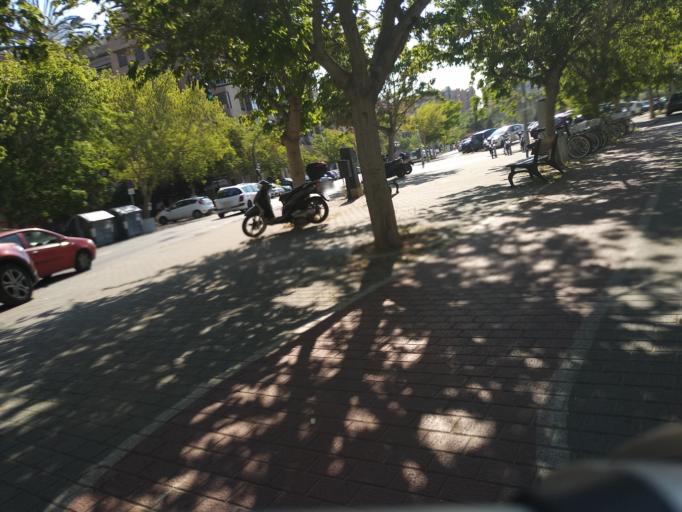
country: ES
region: Valencia
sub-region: Provincia de Valencia
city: Alboraya
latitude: 39.4784
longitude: -0.3471
